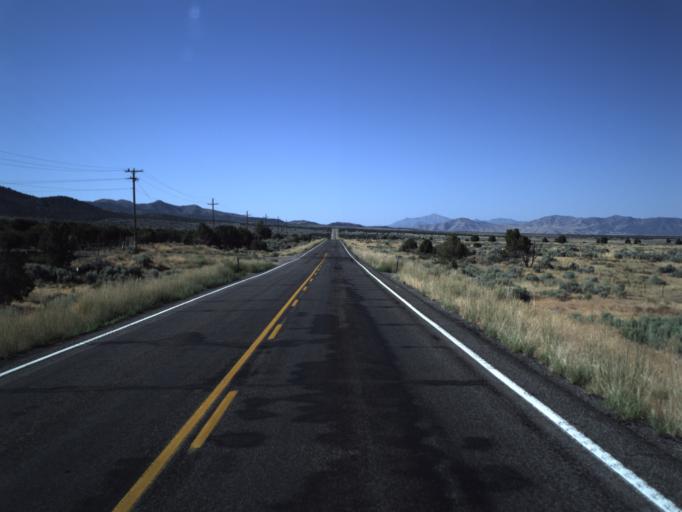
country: US
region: Utah
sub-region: Juab County
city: Mona
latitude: 39.8763
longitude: -112.1381
